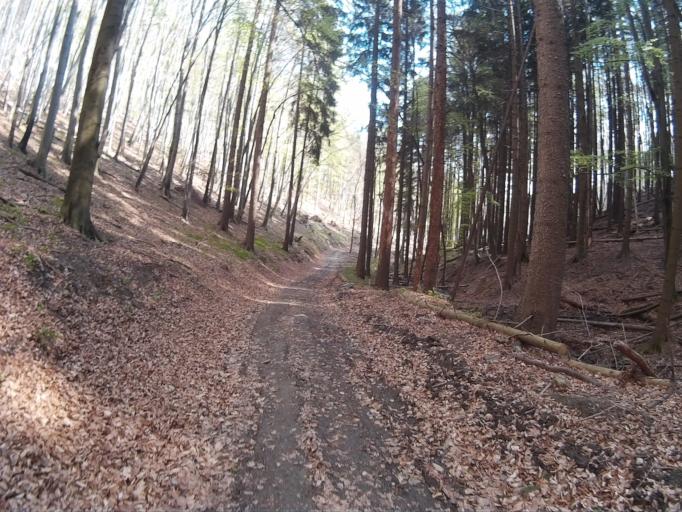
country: AT
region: Burgenland
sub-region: Politischer Bezirk Oberwart
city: Rechnitz
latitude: 47.3467
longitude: 16.4468
